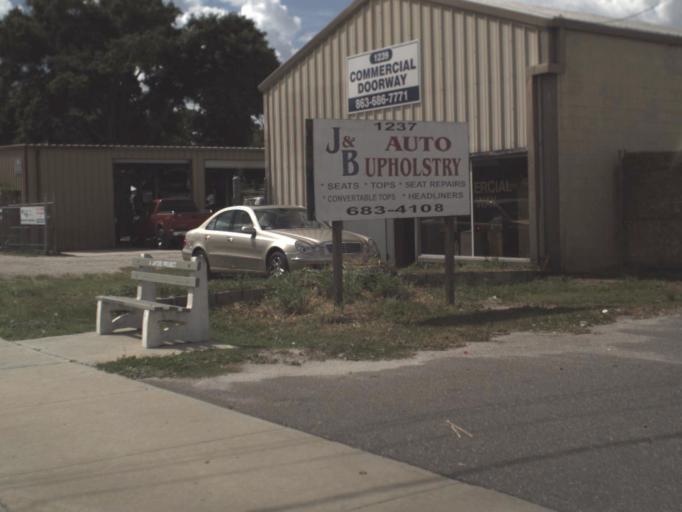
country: US
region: Florida
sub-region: Polk County
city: Lakeland
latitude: 28.0434
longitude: -81.9753
